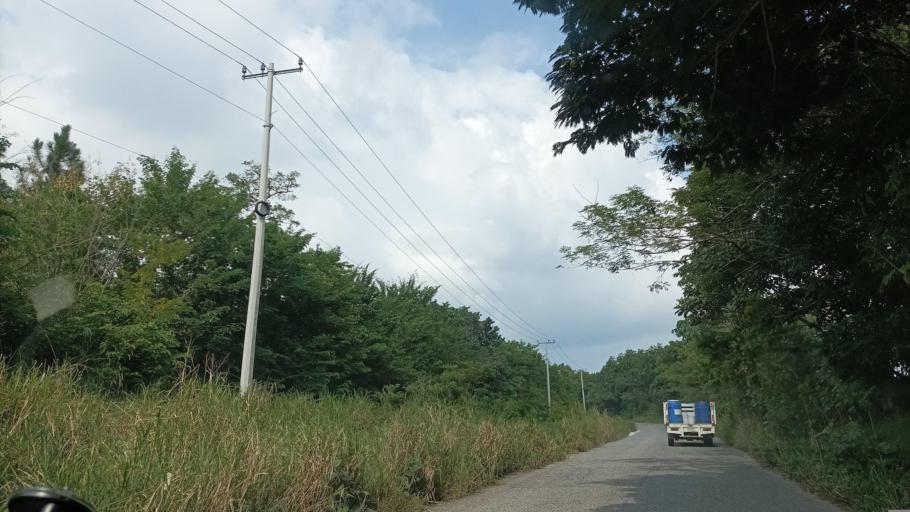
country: MX
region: Veracruz
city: Las Choapas
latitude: 17.8025
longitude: -94.1083
